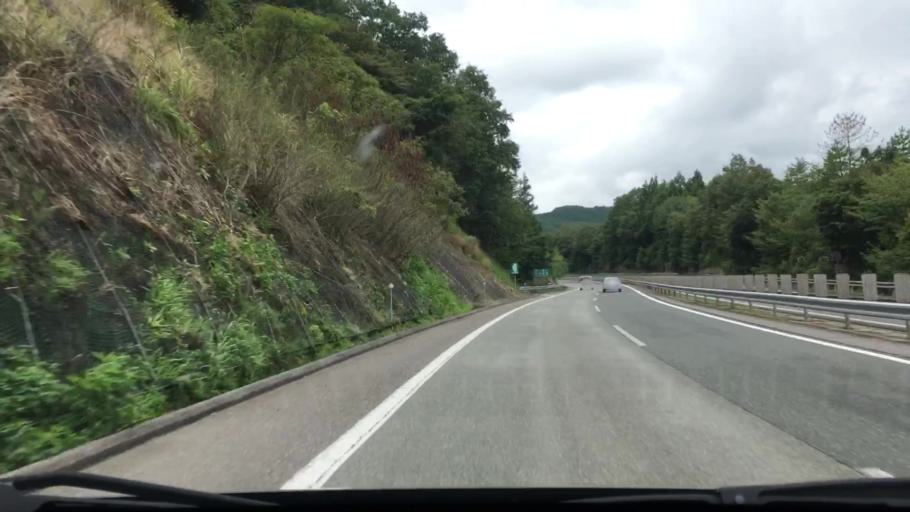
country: JP
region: Hiroshima
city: Miyoshi
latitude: 34.7540
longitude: 132.7713
